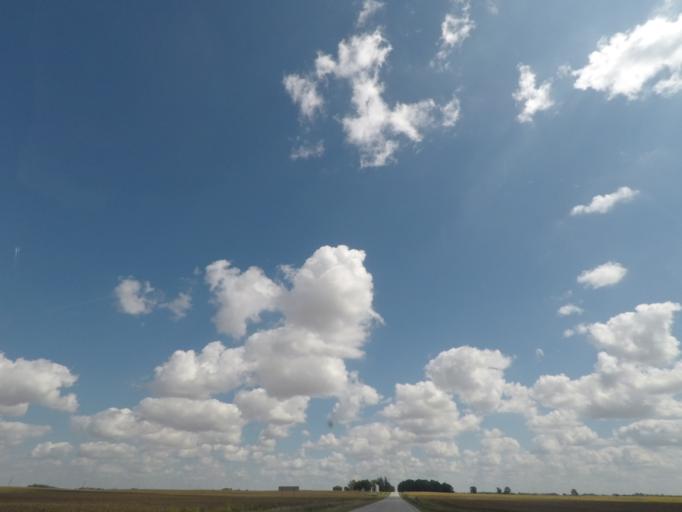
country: US
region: Iowa
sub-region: Story County
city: Nevada
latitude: 42.0779
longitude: -93.3858
